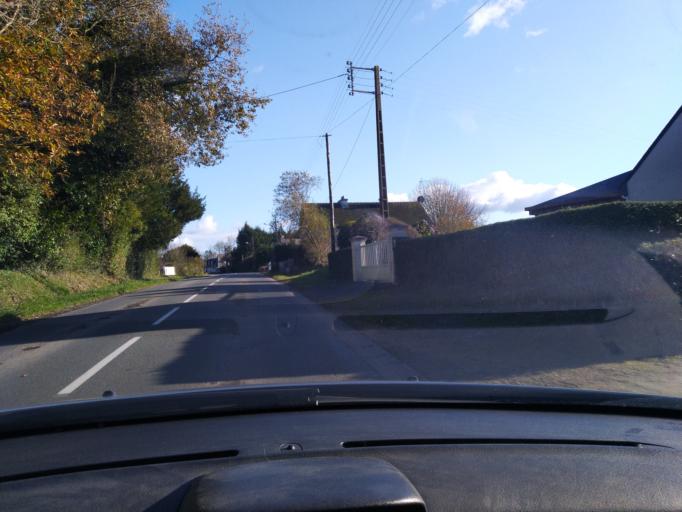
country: FR
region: Brittany
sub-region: Departement des Cotes-d'Armor
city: Plestin-les-Greves
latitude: 48.6428
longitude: -3.6268
